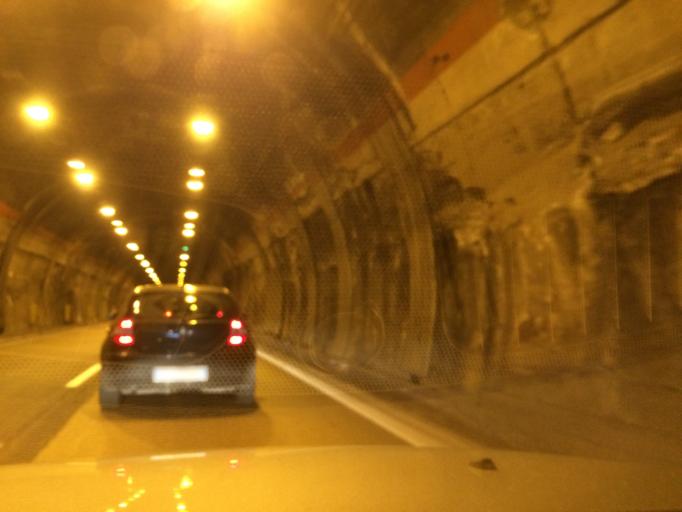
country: IT
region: Umbria
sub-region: Provincia di Perugia
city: Perugia
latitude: 43.0969
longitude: 12.3657
